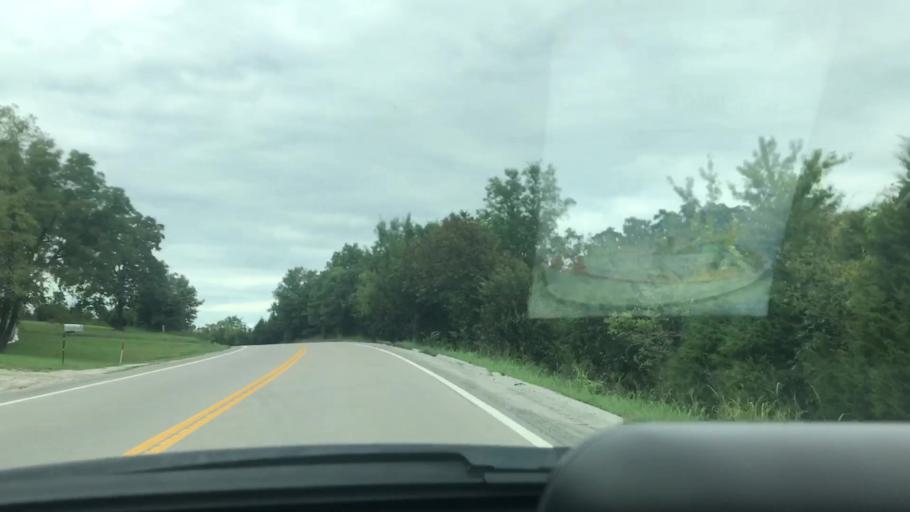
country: US
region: Missouri
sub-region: Benton County
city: Warsaw
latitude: 38.1689
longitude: -93.3099
